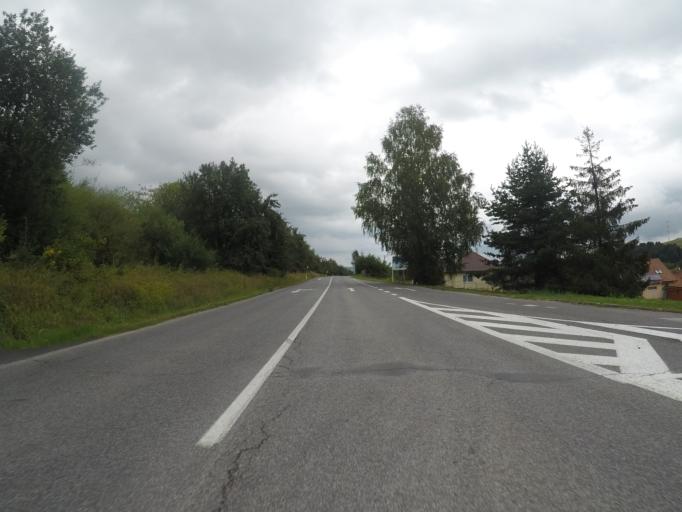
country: SK
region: Kosicky
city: Spisska Nova Ves
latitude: 48.9248
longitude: 20.5420
